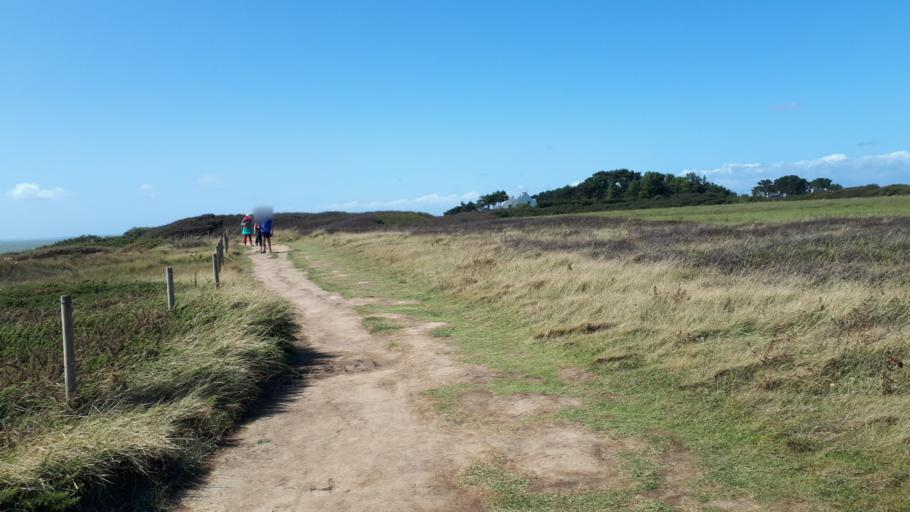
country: FR
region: Brittany
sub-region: Departement du Morbihan
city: Penestin
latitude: 47.4462
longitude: -2.4895
